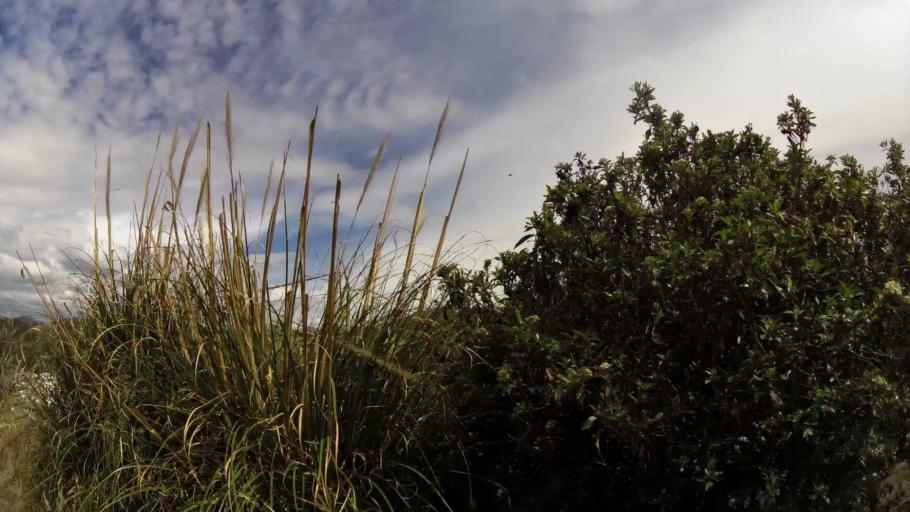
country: EC
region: Cotopaxi
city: Latacunga
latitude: -0.9337
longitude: -78.6057
